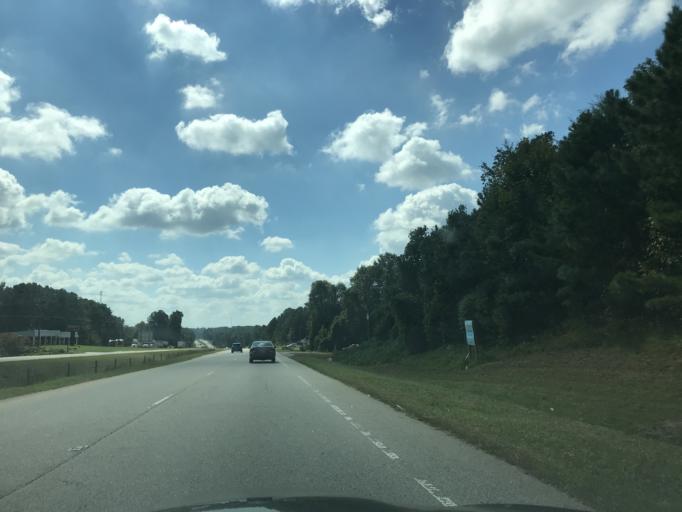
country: US
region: North Carolina
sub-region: Franklin County
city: Franklinton
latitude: 36.0925
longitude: -78.4716
